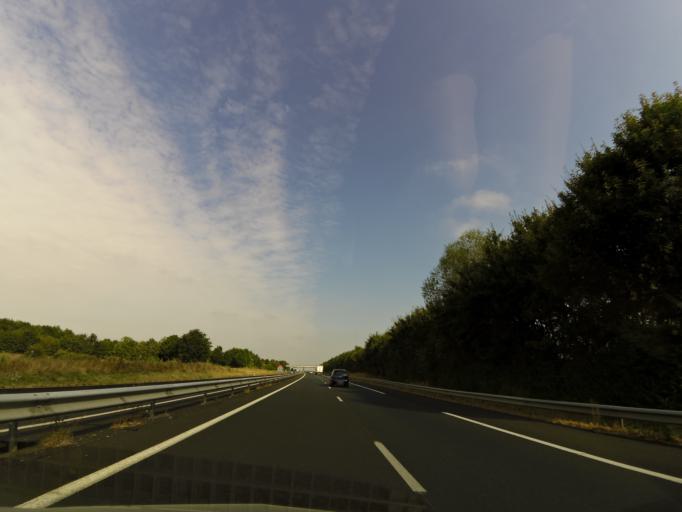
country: FR
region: Pays de la Loire
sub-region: Departement de la Vendee
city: Les Brouzils
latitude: 46.8812
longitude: -1.2891
